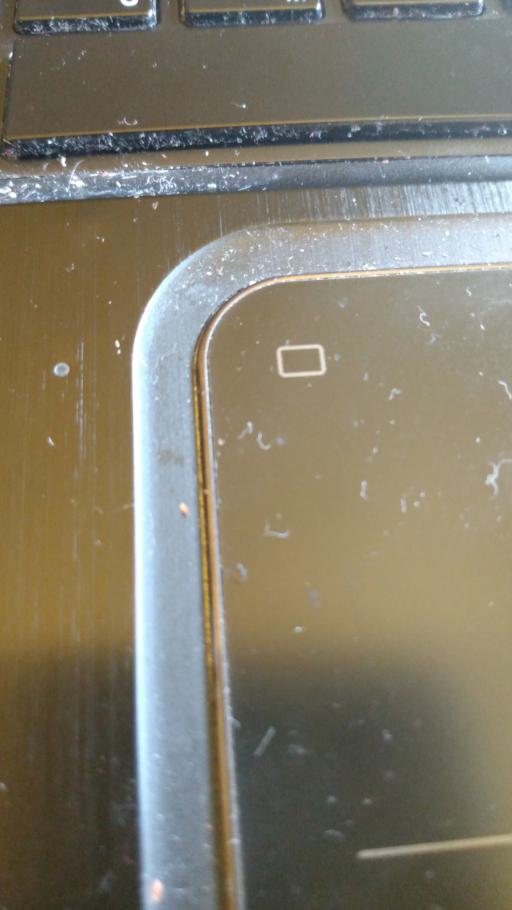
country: RU
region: Moskovskaya
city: Kolomna
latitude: 55.0460
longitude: 38.9061
